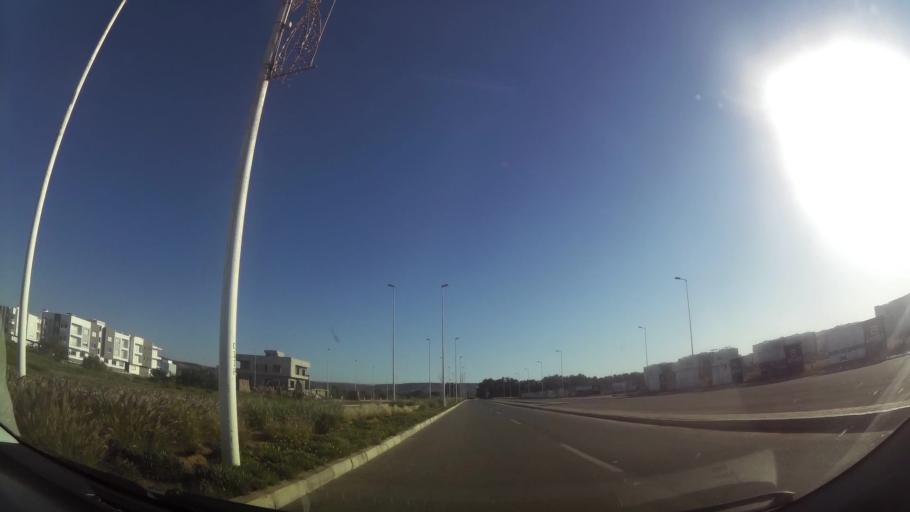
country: MA
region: Oriental
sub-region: Berkane-Taourirt
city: Madagh
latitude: 35.0934
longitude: -2.2602
